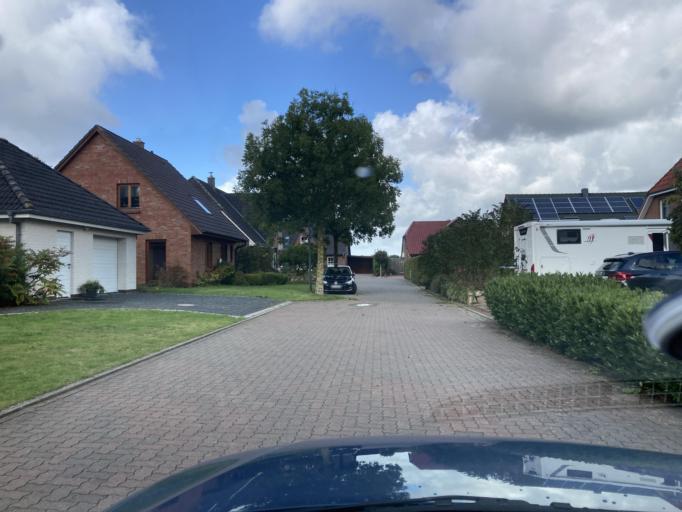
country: DE
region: Schleswig-Holstein
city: Wesseln
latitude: 54.2106
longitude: 9.0799
